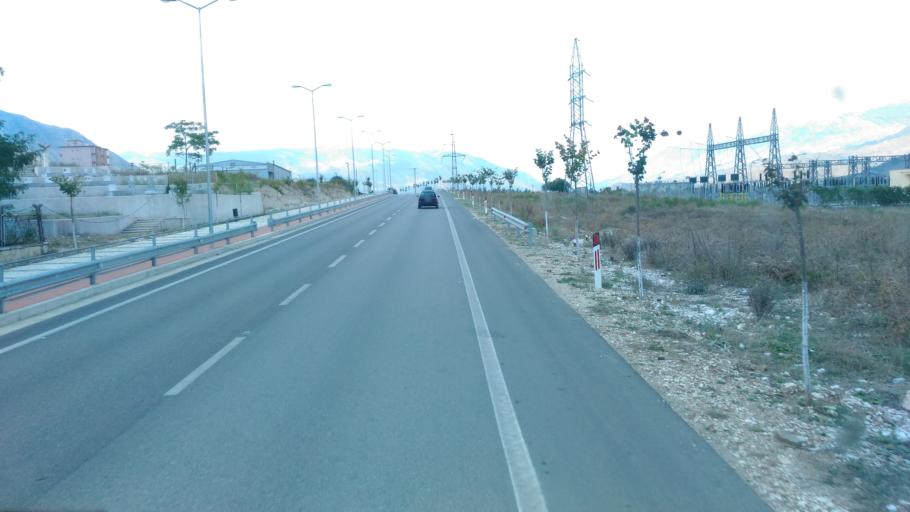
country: AL
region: Gjirokaster
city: Gjirokaster
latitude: 40.0920
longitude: 20.1368
